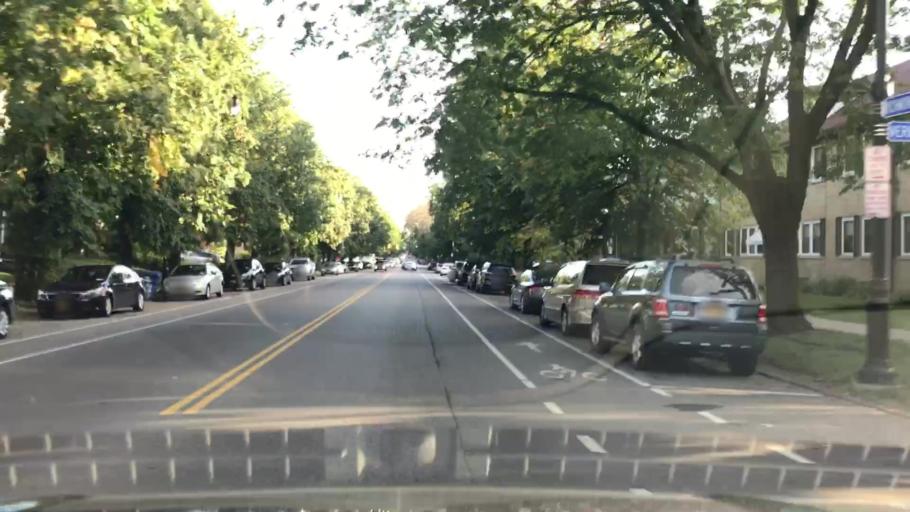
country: US
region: New York
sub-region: Erie County
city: Buffalo
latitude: 42.9109
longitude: -78.8821
